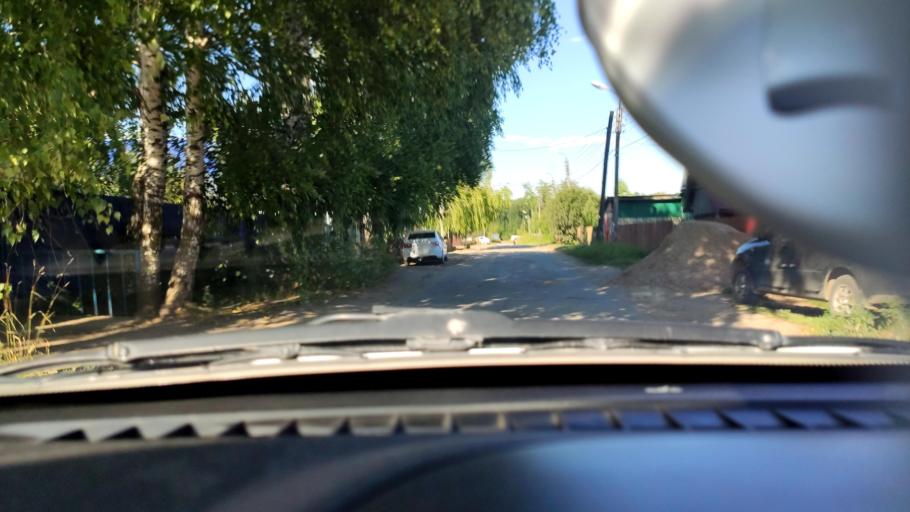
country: RU
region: Perm
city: Krasnokamsk
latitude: 58.0772
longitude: 55.8106
